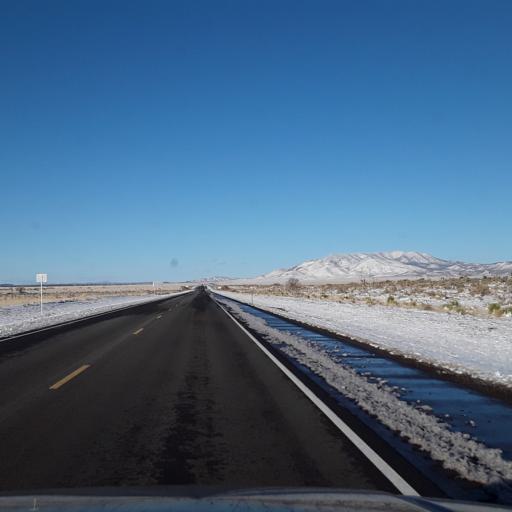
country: US
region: New Mexico
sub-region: Lincoln County
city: Carrizozo
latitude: 33.6567
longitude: -105.8620
